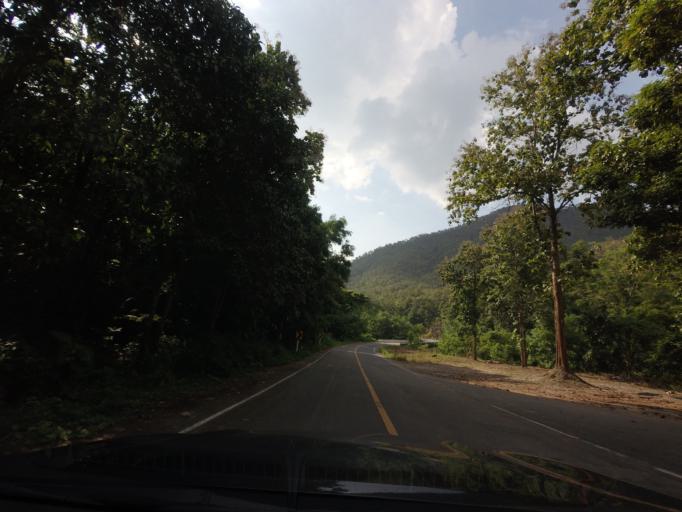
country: TH
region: Nan
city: Na Noi
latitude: 18.3116
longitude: 100.9051
